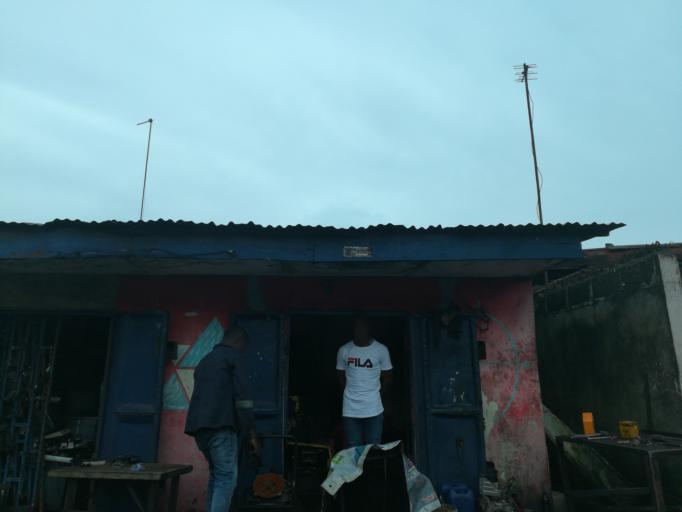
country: NG
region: Rivers
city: Port Harcourt
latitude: 4.7966
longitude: 6.9917
